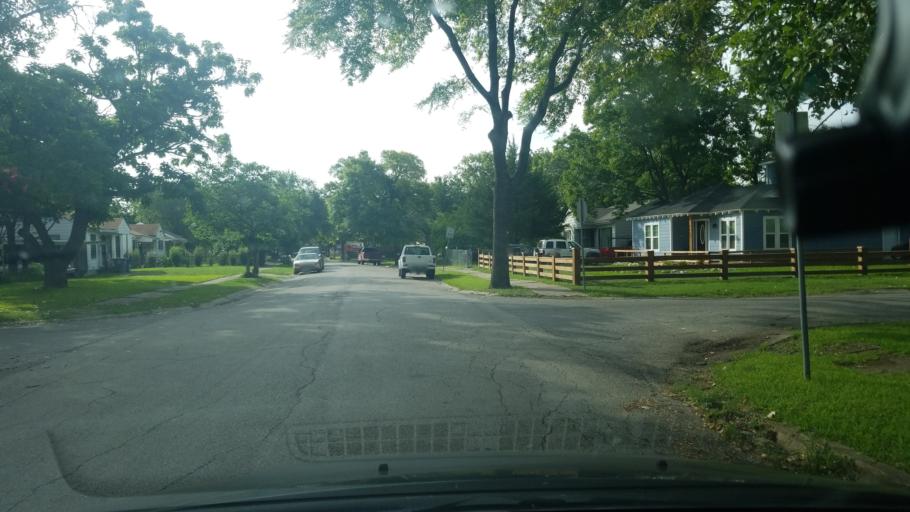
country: US
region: Texas
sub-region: Dallas County
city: Balch Springs
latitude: 32.7364
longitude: -96.6709
